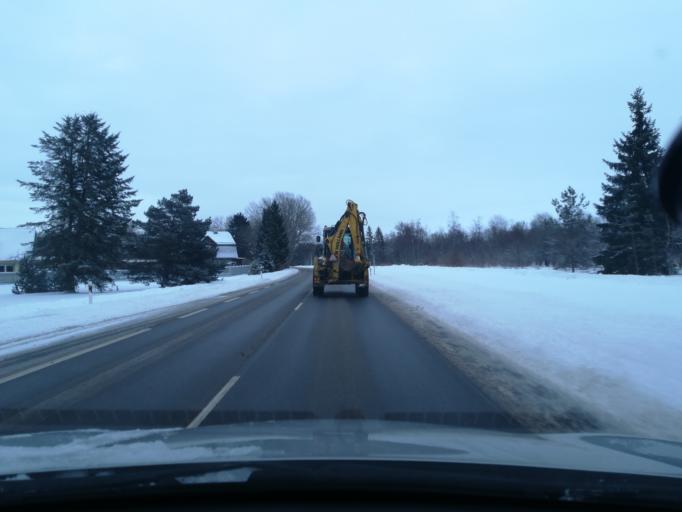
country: EE
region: Harju
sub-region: Keila linn
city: Keila
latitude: 59.3946
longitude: 24.2814
